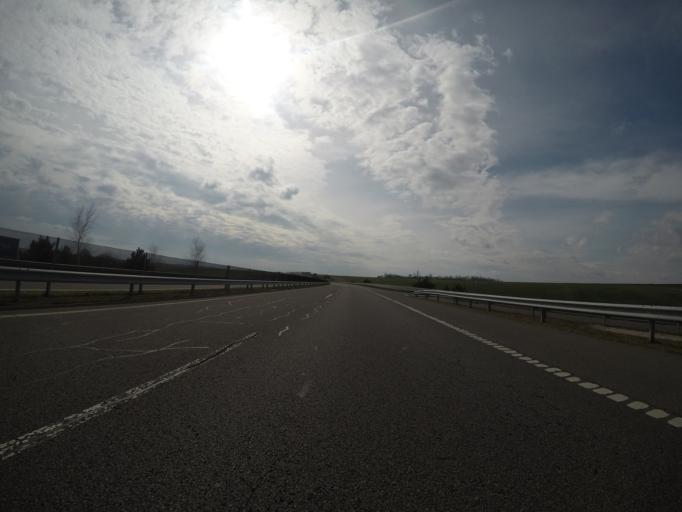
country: HU
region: Baranya
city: Lanycsok
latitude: 46.1115
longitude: 18.5903
